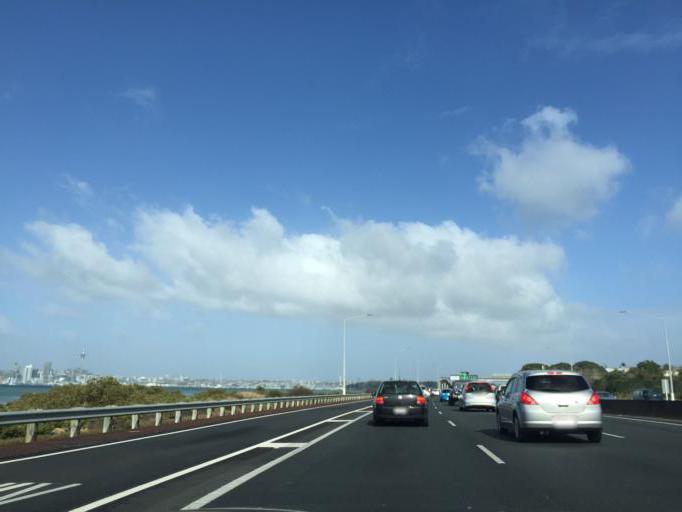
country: NZ
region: Auckland
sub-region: Auckland
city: North Shore
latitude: -36.8052
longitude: 174.7599
